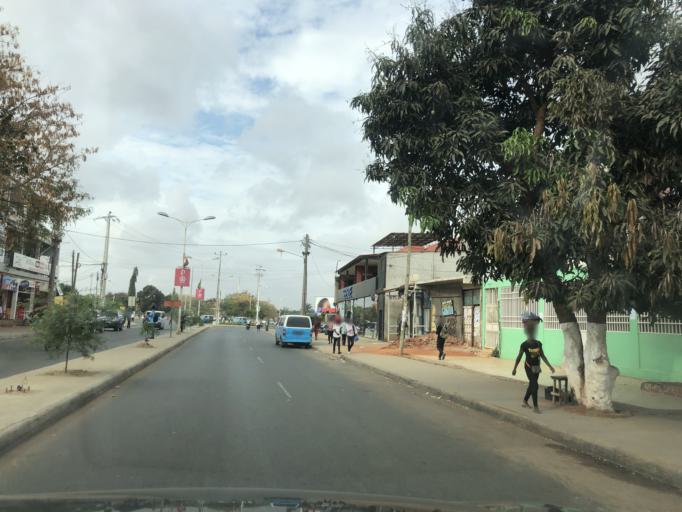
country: AO
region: Luanda
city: Luanda
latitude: -8.9107
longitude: 13.3719
